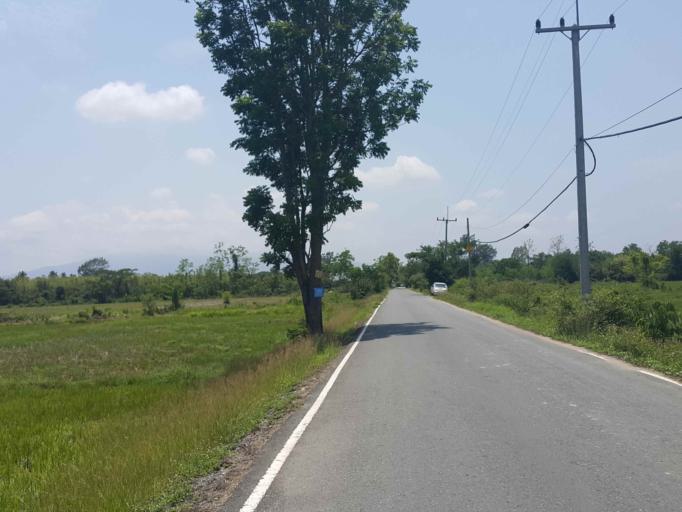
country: TH
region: Chiang Mai
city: San Sai
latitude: 18.8066
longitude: 99.0860
